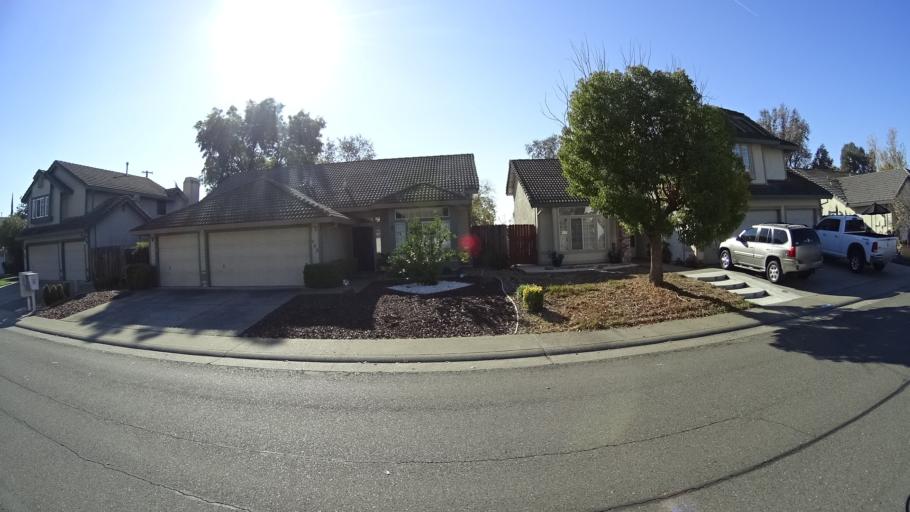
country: US
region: California
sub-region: Sacramento County
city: Citrus Heights
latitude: 38.7224
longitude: -121.3045
